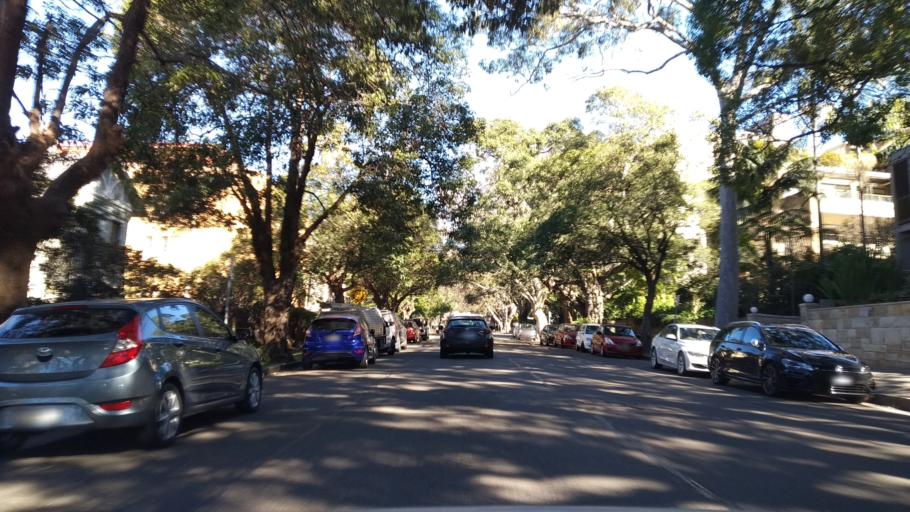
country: AU
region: New South Wales
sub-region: Woollahra
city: Darling Point
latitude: -33.8763
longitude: 151.2393
